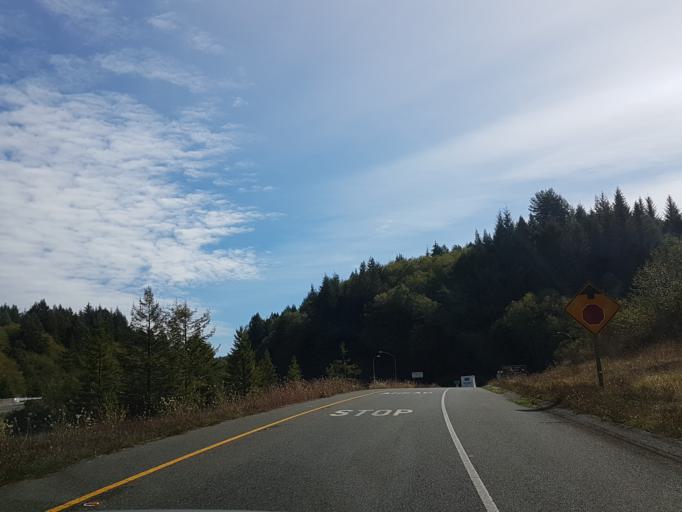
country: US
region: California
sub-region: Del Norte County
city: Bertsch-Oceanview
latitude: 41.4676
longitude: -124.0401
